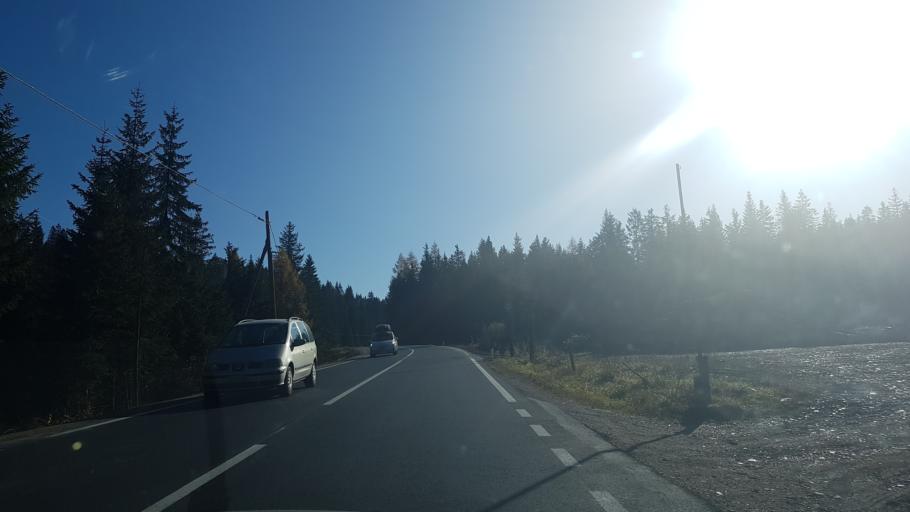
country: IT
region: Trentino-Alto Adige
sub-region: Bolzano
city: Sesto
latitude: 46.6583
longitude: 12.4140
